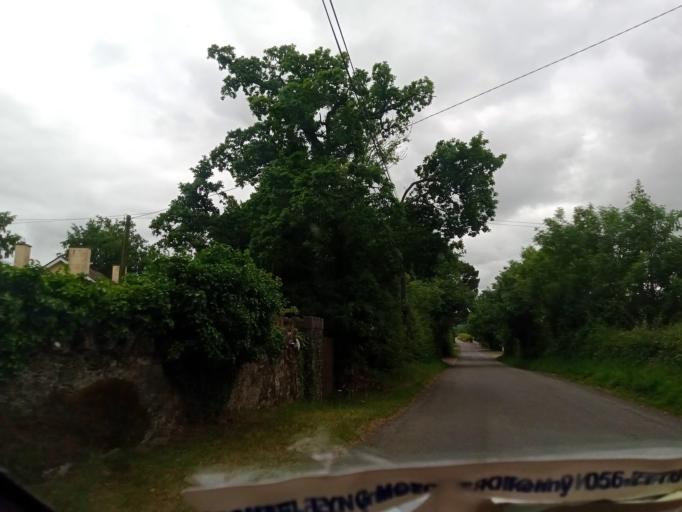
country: IE
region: Leinster
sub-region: Kilkenny
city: Ballyragget
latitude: 52.7421
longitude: -7.4171
